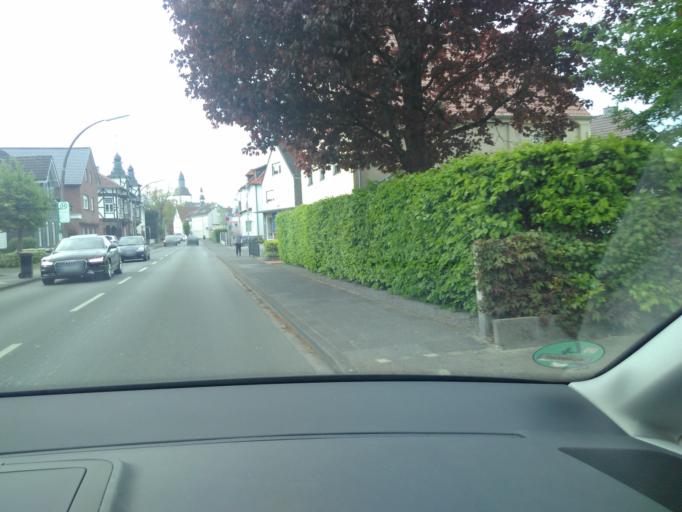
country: DE
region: North Rhine-Westphalia
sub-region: Regierungsbezirk Detmold
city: Rheda-Wiedenbruck
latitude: 51.8342
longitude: 8.3174
